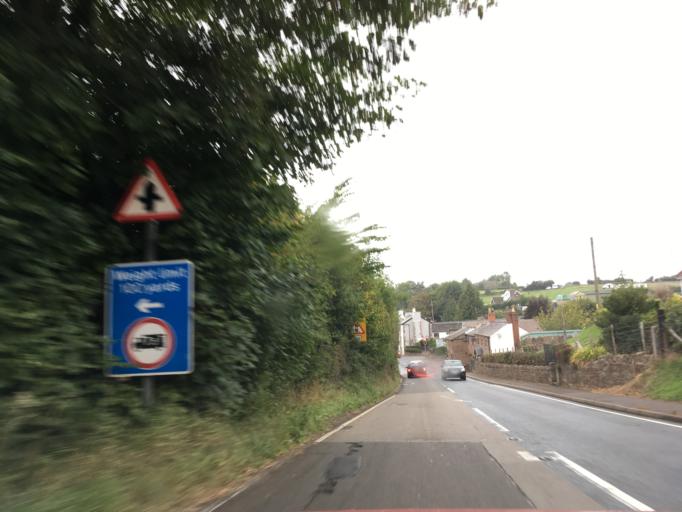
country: GB
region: England
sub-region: Herefordshire
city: Lea
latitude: 51.8928
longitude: -2.4904
